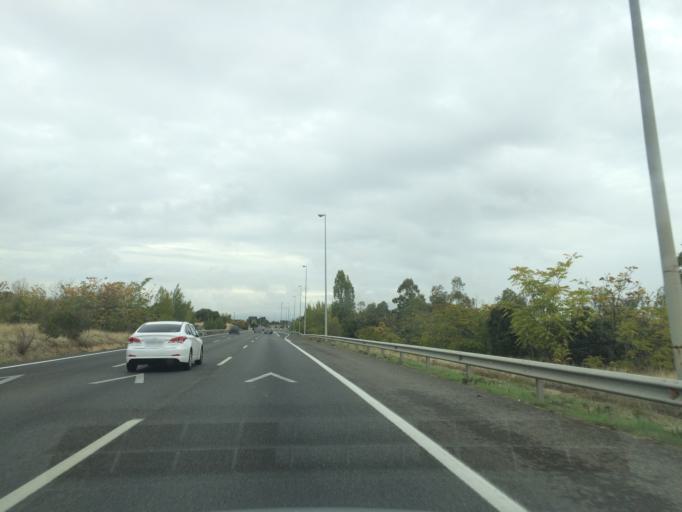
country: ES
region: Madrid
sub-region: Provincia de Madrid
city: Tres Cantos
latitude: 40.5661
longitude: -3.7101
